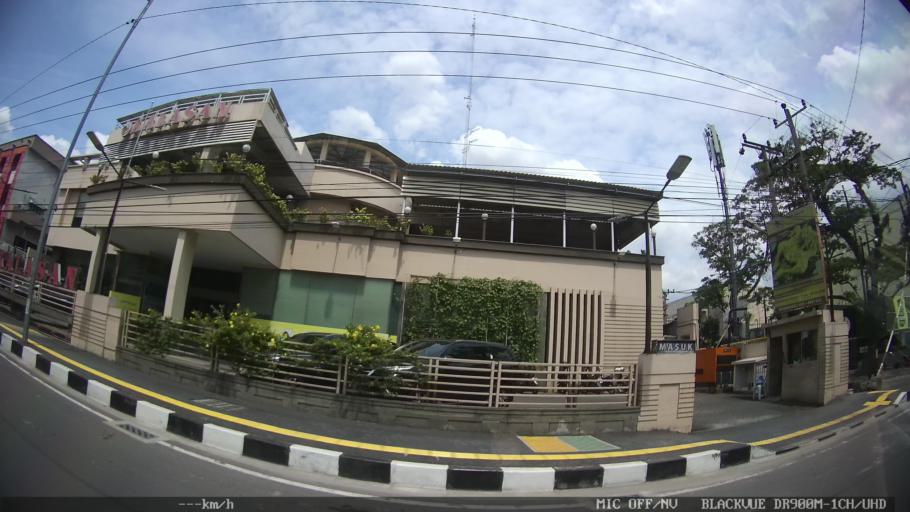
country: ID
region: North Sumatra
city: Medan
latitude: 3.5887
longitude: 98.6614
